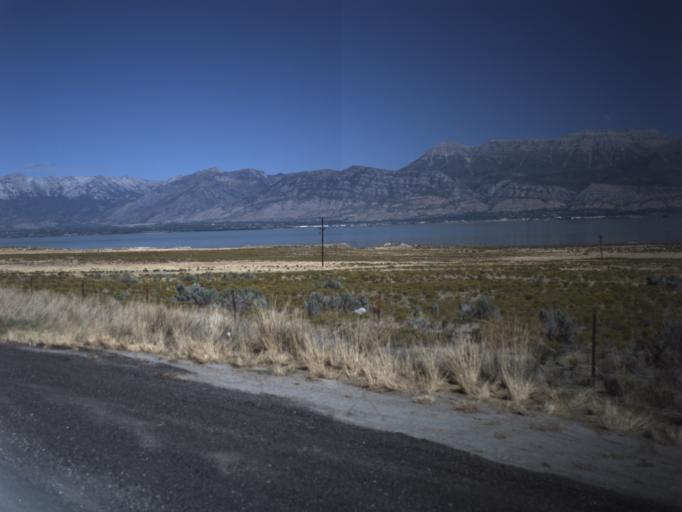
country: US
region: Utah
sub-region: Utah County
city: Saratoga Springs
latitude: 40.2629
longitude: -111.8671
